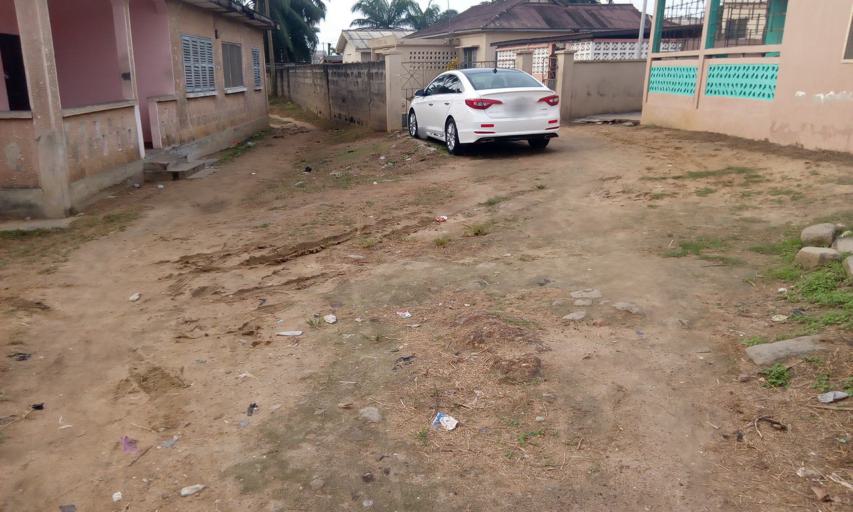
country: GH
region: Central
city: Winneba
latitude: 5.3568
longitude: -0.6290
